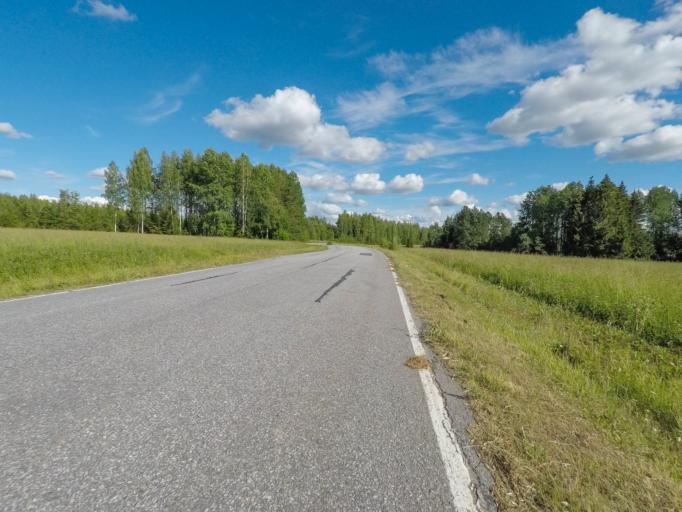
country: FI
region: South Karelia
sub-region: Imatra
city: Imatra
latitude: 61.1351
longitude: 28.6571
